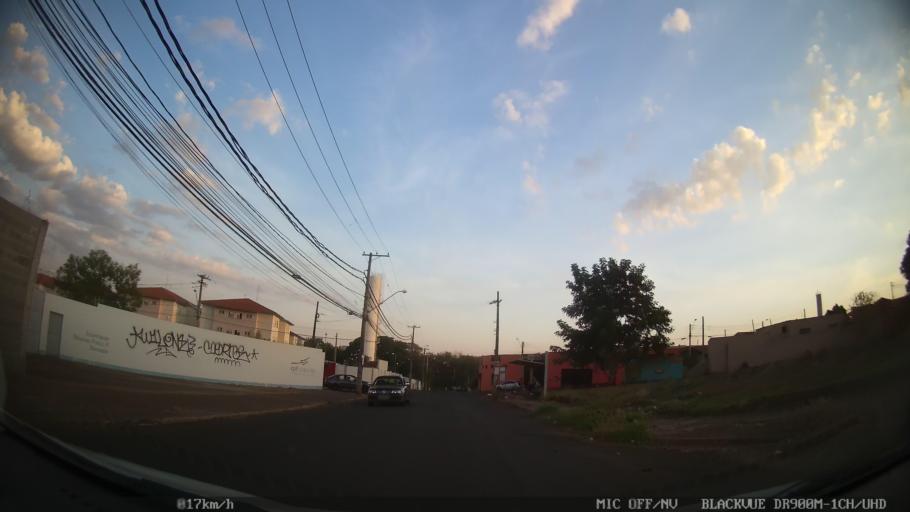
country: BR
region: Sao Paulo
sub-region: Ribeirao Preto
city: Ribeirao Preto
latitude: -21.1204
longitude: -47.8177
